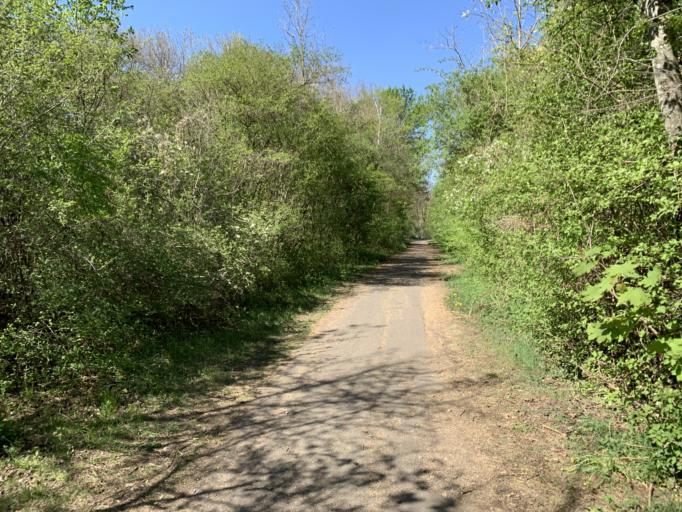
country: DE
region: Bavaria
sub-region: Swabia
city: Gersthofen
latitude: 48.4294
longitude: 10.8916
